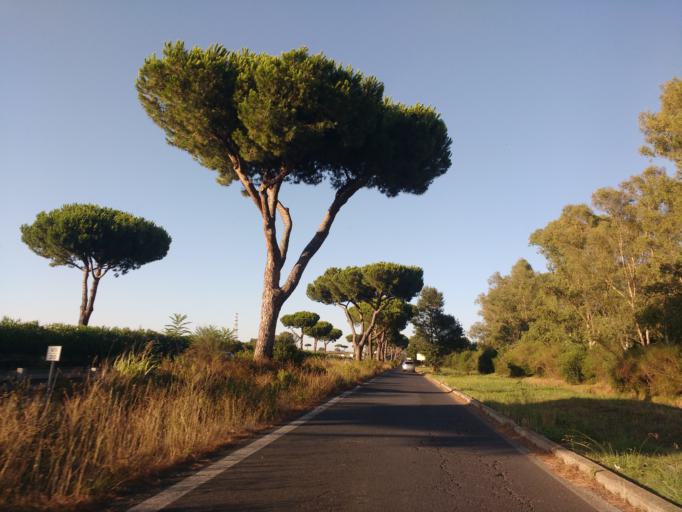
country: IT
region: Latium
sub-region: Citta metropolitana di Roma Capitale
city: Acilia-Castel Fusano-Ostia Antica
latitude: 41.7583
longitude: 12.3745
